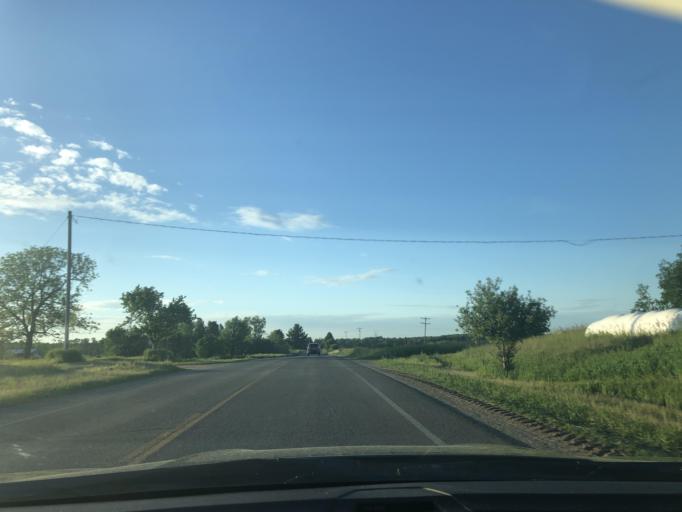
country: US
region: Michigan
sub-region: Missaukee County
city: Lake City
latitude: 44.4271
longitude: -85.0752
